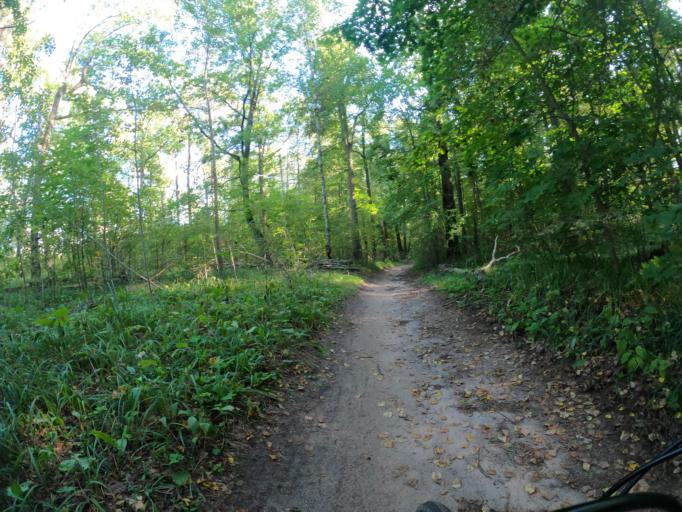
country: RU
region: Moskovskaya
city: Stupino
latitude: 54.8728
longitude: 38.0980
